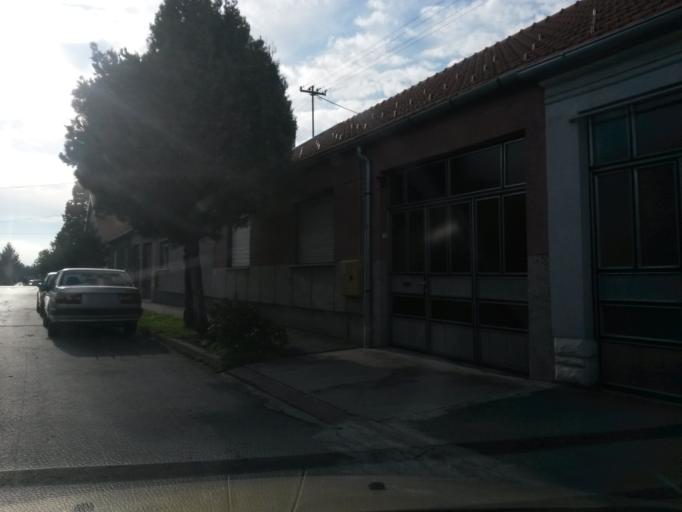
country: HR
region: Osjecko-Baranjska
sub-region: Grad Osijek
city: Osijek
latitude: 45.5495
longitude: 18.7071
